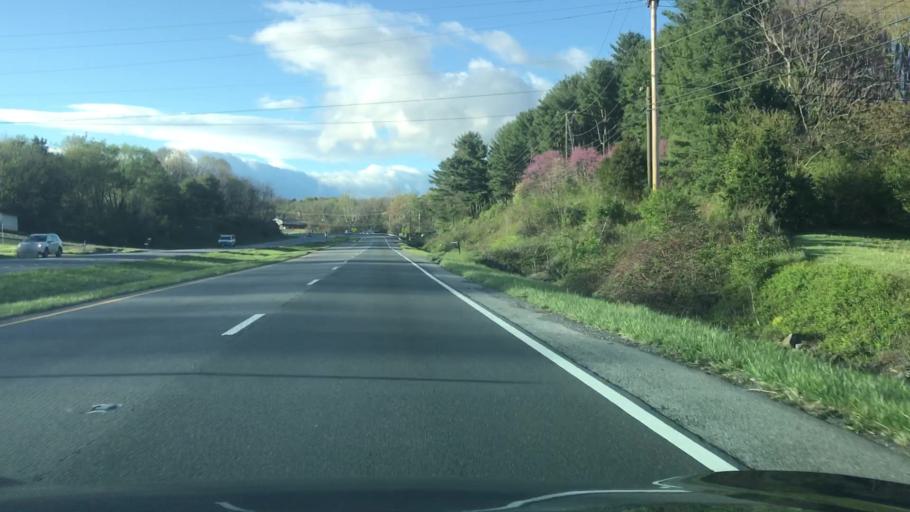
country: US
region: Virginia
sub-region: Botetourt County
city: Cloverdale
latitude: 37.3716
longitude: -79.8863
